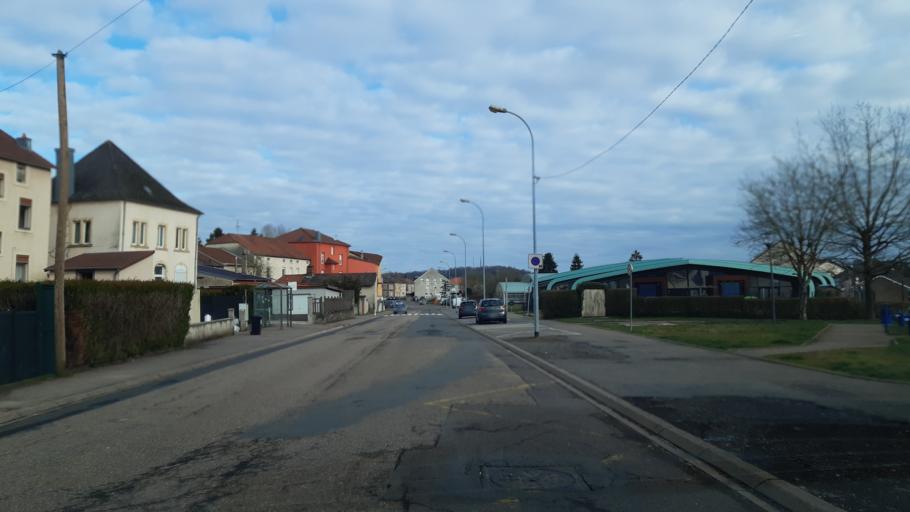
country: FR
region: Lorraine
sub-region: Departement de la Moselle
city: Audun-le-Tiche
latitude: 49.4676
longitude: 5.9546
